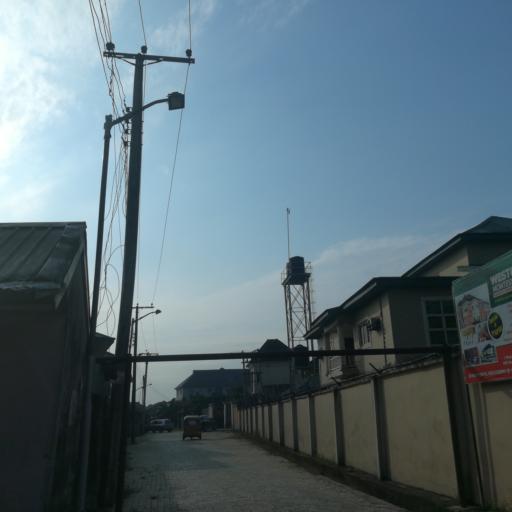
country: NG
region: Rivers
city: Port Harcourt
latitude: 4.8560
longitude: 6.9642
